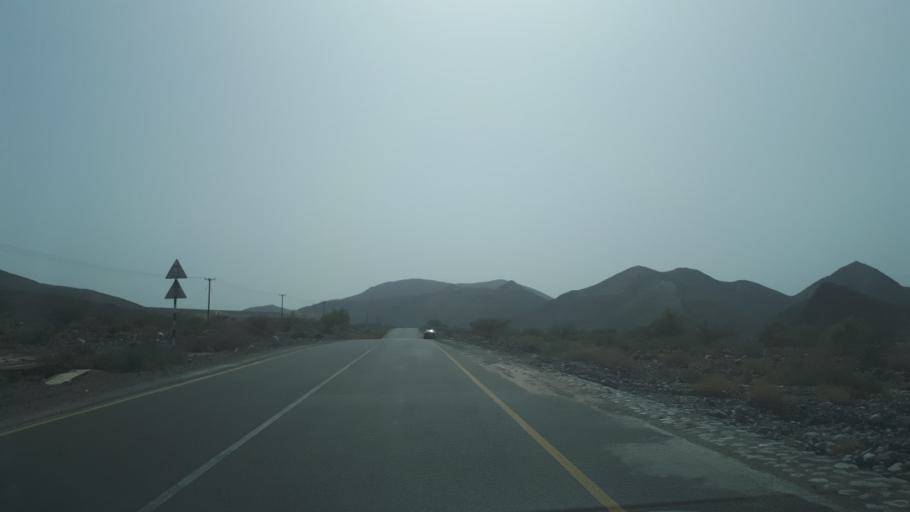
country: OM
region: Muhafazat ad Dakhiliyah
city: Bahla'
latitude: 23.2231
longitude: 56.9944
